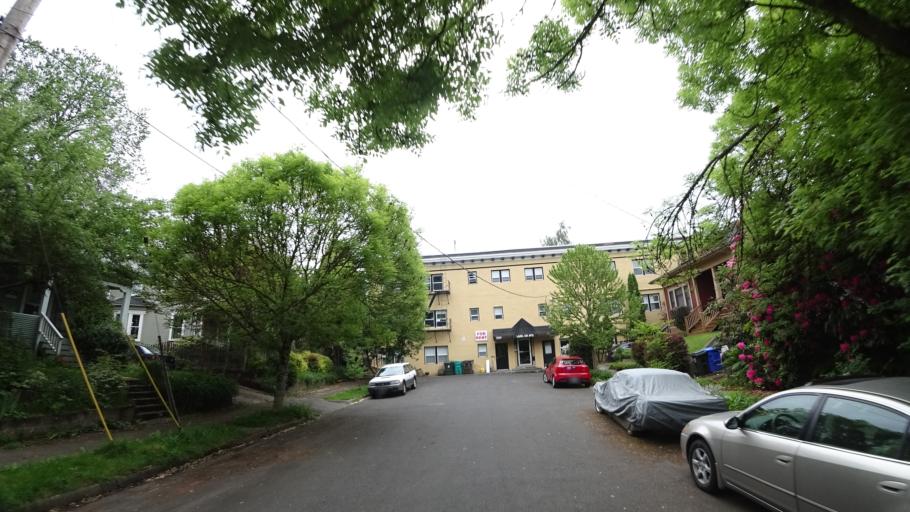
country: US
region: Oregon
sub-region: Multnomah County
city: Portland
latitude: 45.5214
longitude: -122.6359
